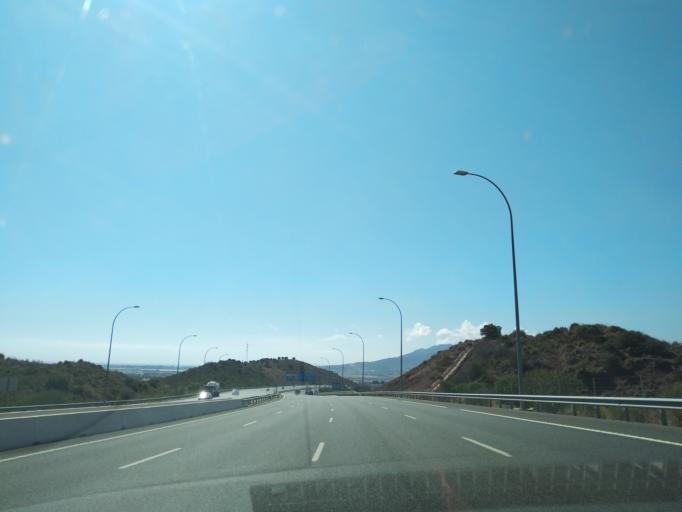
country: ES
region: Andalusia
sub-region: Provincia de Malaga
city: Alhaurin de la Torre
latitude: 36.7327
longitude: -4.5075
